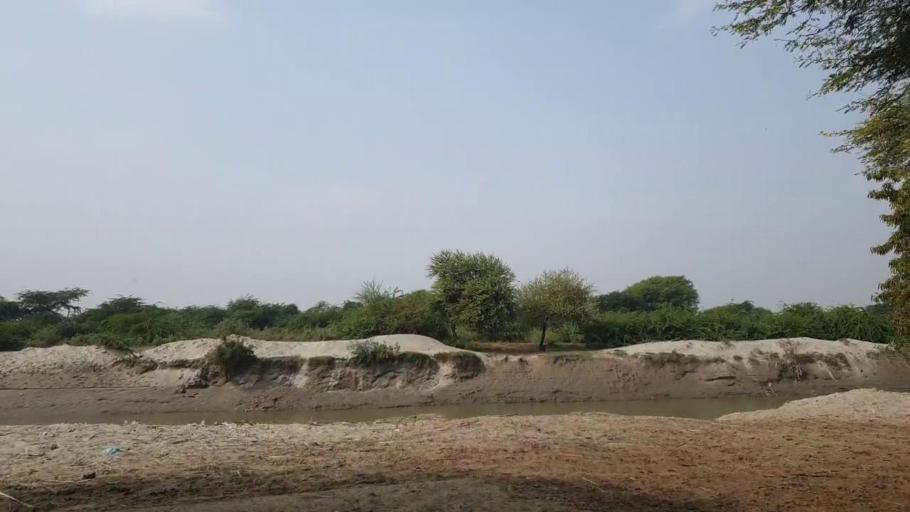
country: PK
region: Sindh
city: Kario
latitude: 24.7585
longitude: 68.5250
